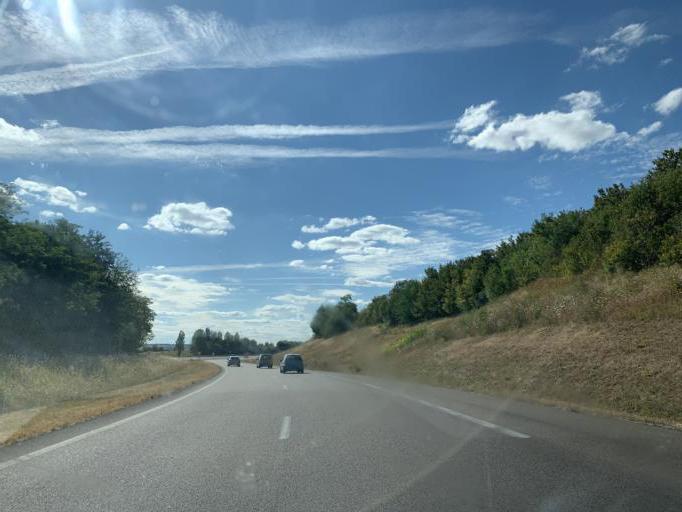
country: FR
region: Bourgogne
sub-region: Departement de l'Yonne
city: Soucy
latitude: 48.2717
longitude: 3.2901
